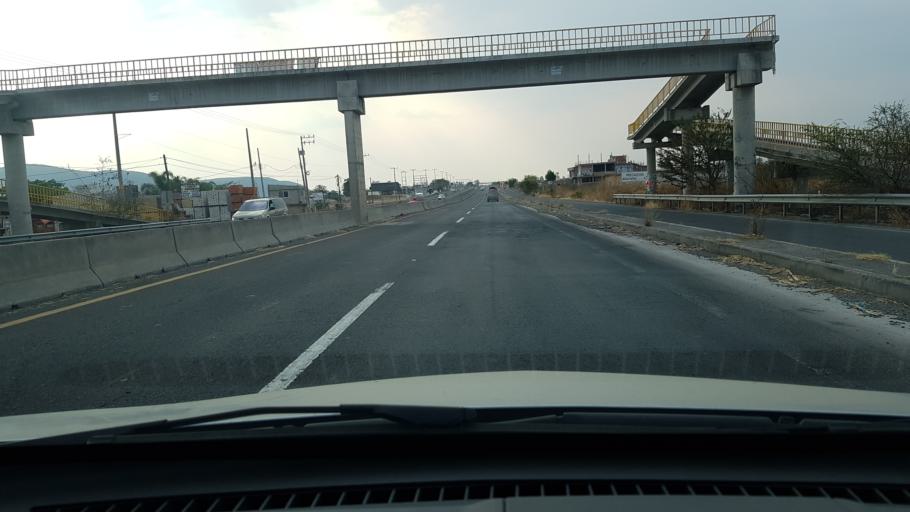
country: MX
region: Morelos
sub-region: Ayala
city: Unidad Habitacional Mariano Matamoros
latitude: 18.7383
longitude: -98.8263
